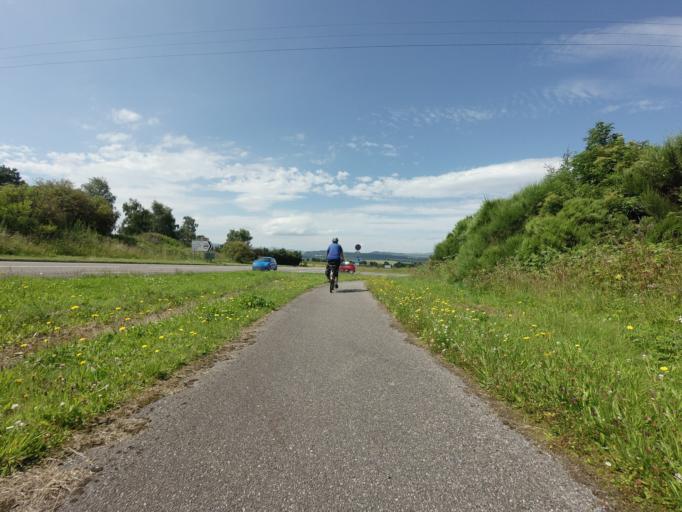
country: GB
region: Scotland
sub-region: Highland
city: Conon Bridge
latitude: 57.5512
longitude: -4.4049
